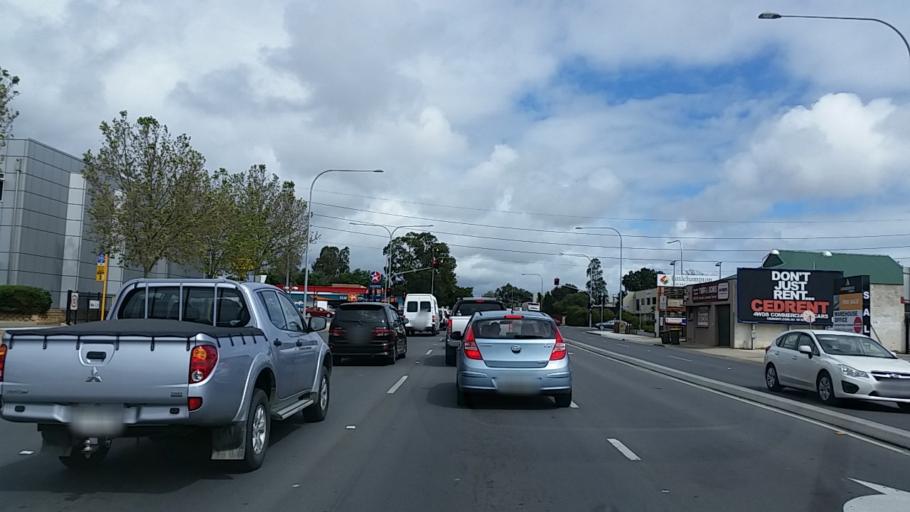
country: AU
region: South Australia
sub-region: Unley
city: Forestville
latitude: -34.9411
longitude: 138.5710
